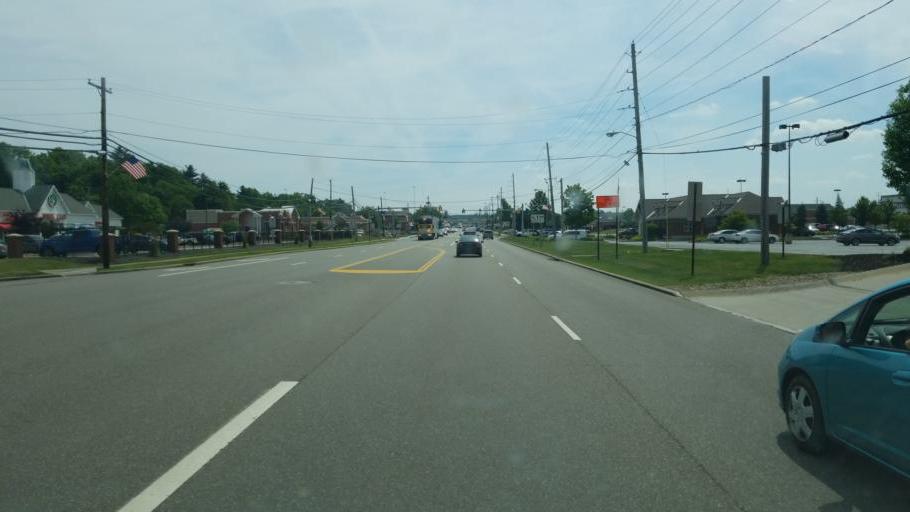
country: US
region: Ohio
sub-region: Summit County
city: Macedonia
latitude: 41.3139
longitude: -81.5215
